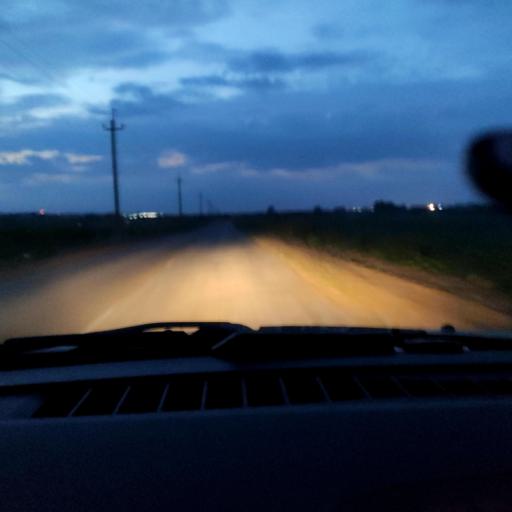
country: RU
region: Perm
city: Kultayevo
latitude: 57.8906
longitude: 55.9905
